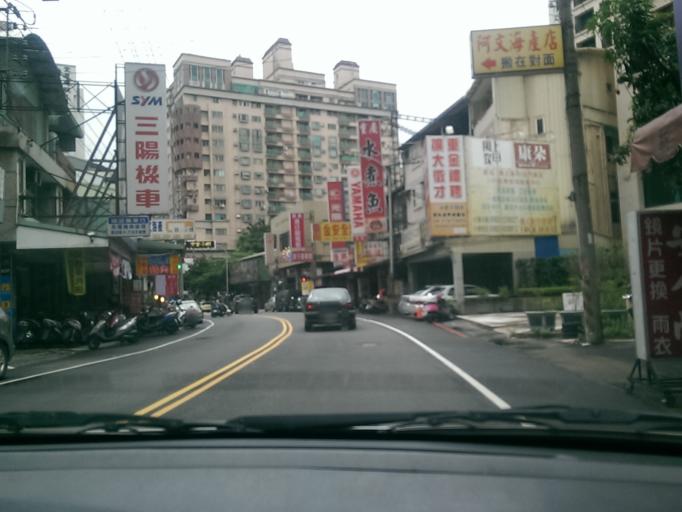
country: TW
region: Taiwan
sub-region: Taichung City
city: Taichung
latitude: 24.1738
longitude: 120.6445
